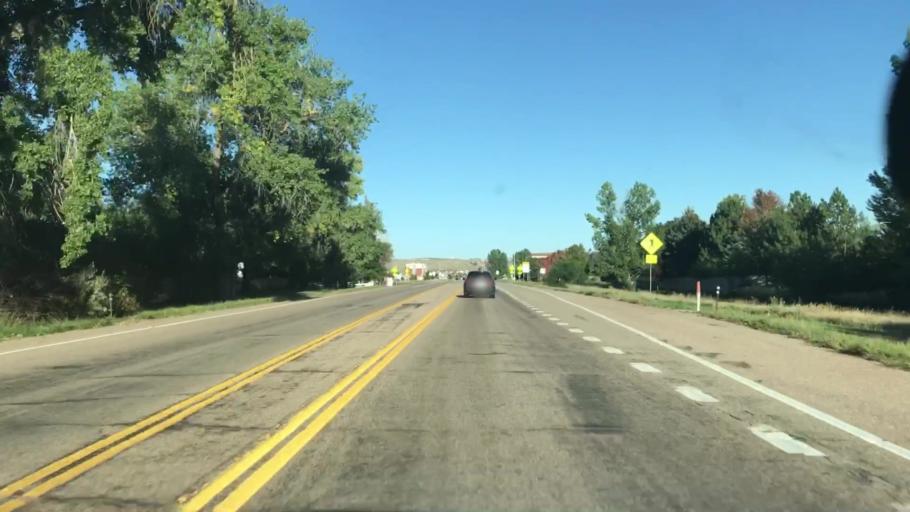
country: US
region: Colorado
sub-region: Boulder County
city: Lafayette
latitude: 39.9723
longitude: -105.0975
